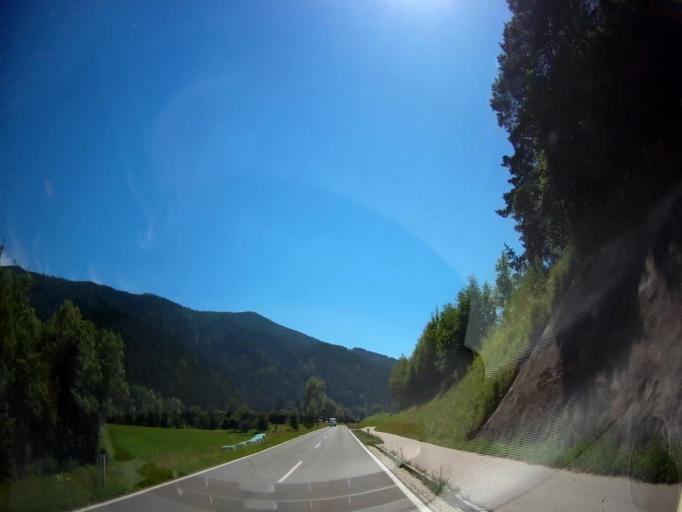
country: AT
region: Carinthia
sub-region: Politischer Bezirk Sankt Veit an der Glan
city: Gurk
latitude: 46.8668
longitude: 14.2547
